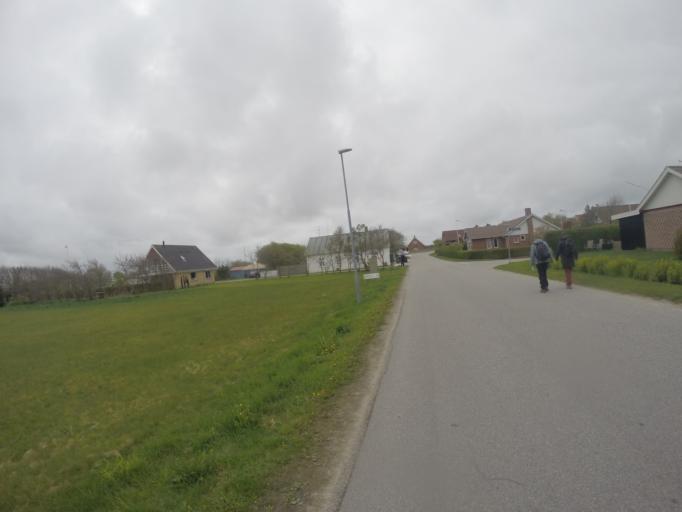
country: DK
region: North Denmark
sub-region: Thisted Kommune
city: Hurup
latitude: 56.9198
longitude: 8.3601
